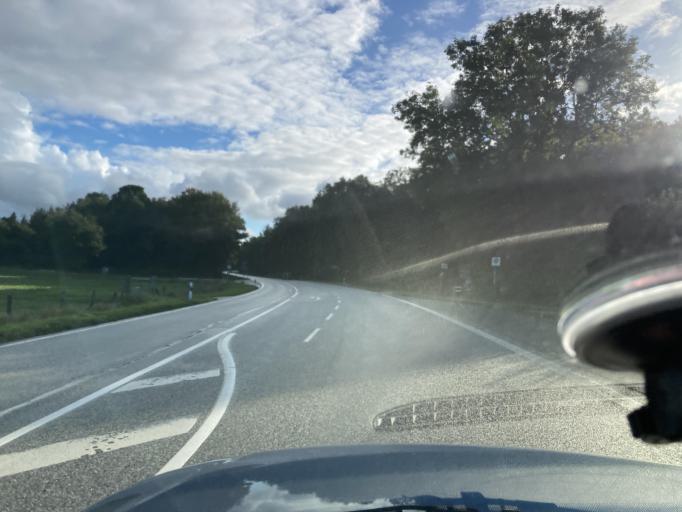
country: DE
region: Schleswig-Holstein
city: Fockbek
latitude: 54.2807
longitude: 9.5735
